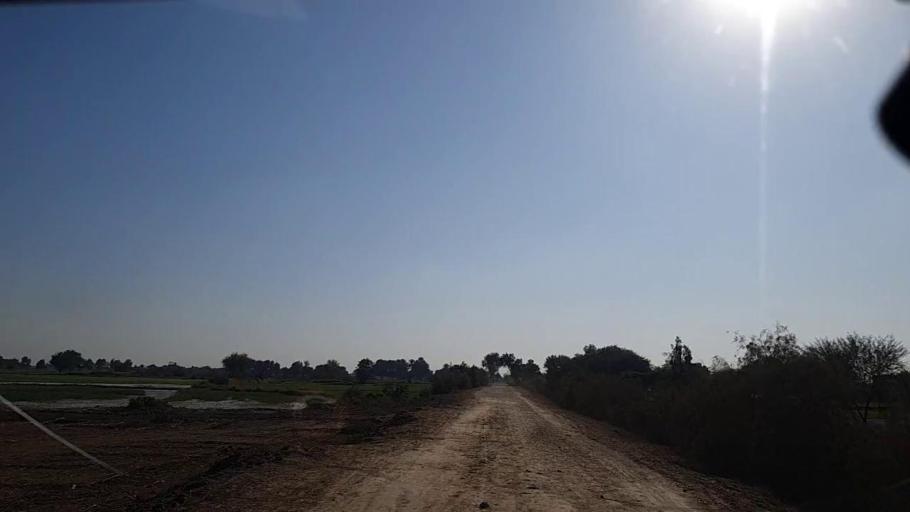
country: PK
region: Sindh
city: Khanpur
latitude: 27.7895
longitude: 69.3700
